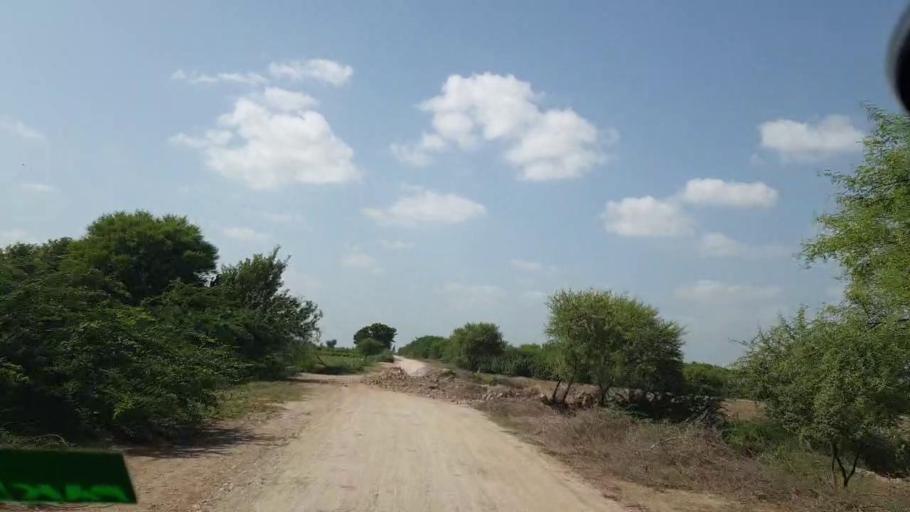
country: PK
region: Sindh
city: Naukot
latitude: 24.6474
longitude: 69.2219
